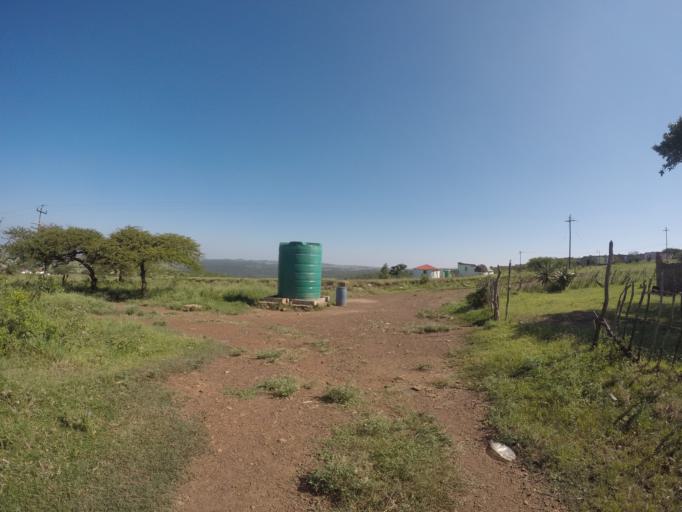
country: ZA
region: KwaZulu-Natal
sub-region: uThungulu District Municipality
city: Empangeni
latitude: -28.5709
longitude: 31.7166
